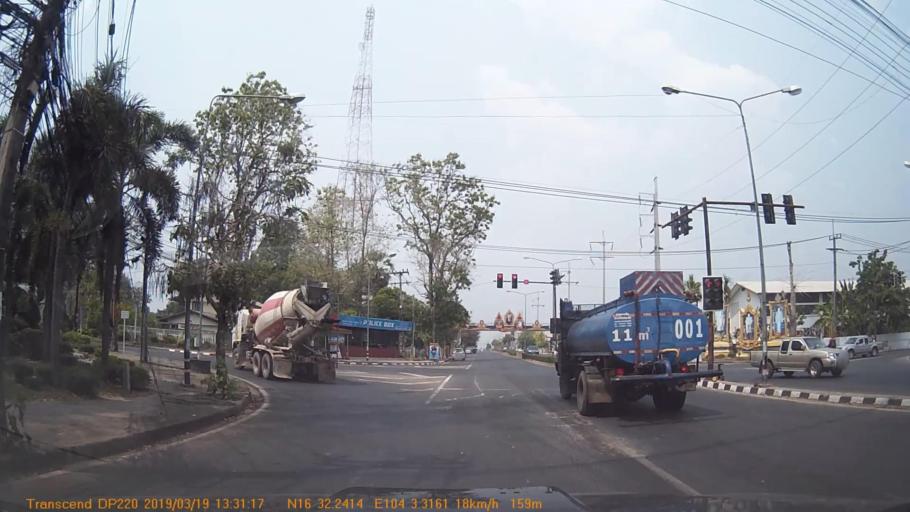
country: TH
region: Kalasin
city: Kuchinarai
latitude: 16.5375
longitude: 104.0553
